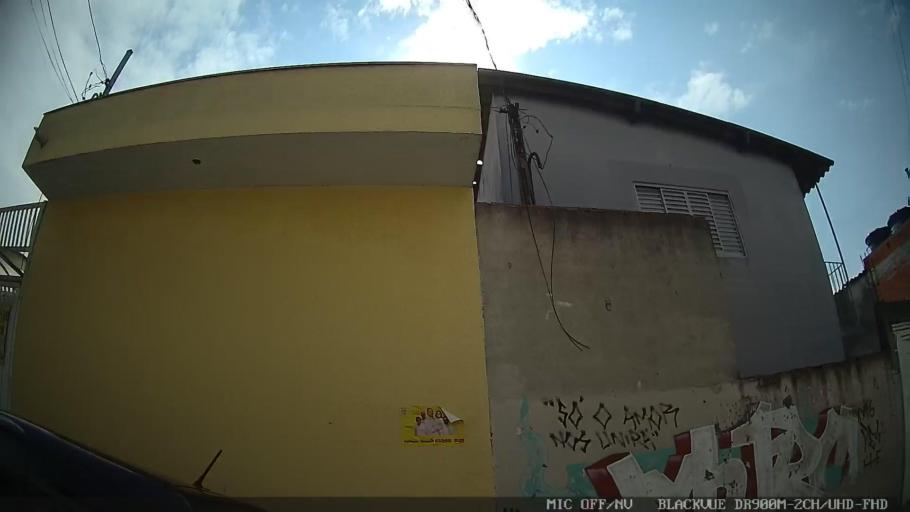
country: BR
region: Sao Paulo
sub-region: Ferraz De Vasconcelos
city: Ferraz de Vasconcelos
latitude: -23.5027
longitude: -46.4152
